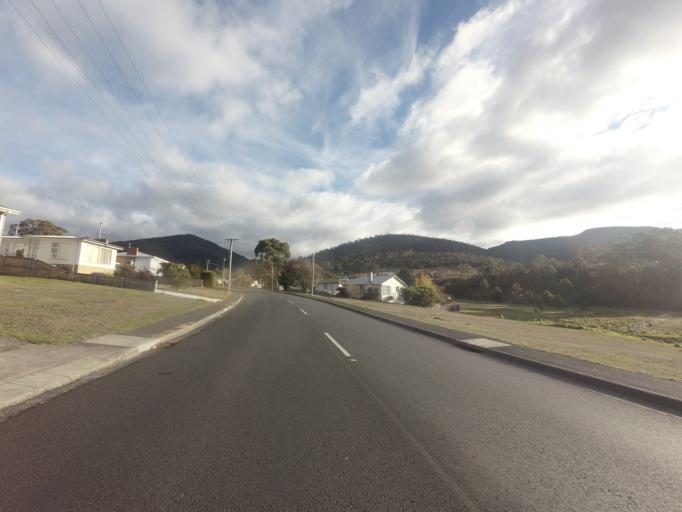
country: AU
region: Tasmania
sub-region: Glenorchy
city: Berriedale
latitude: -42.8038
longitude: 147.2458
